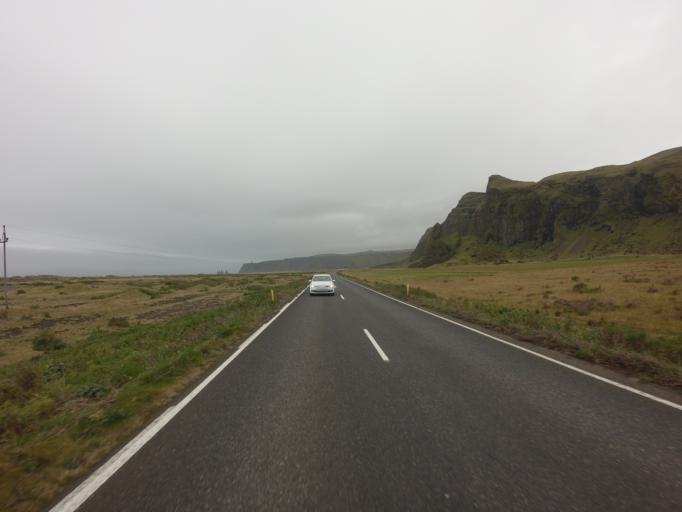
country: IS
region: South
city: Vestmannaeyjar
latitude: 63.4191
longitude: -18.9493
